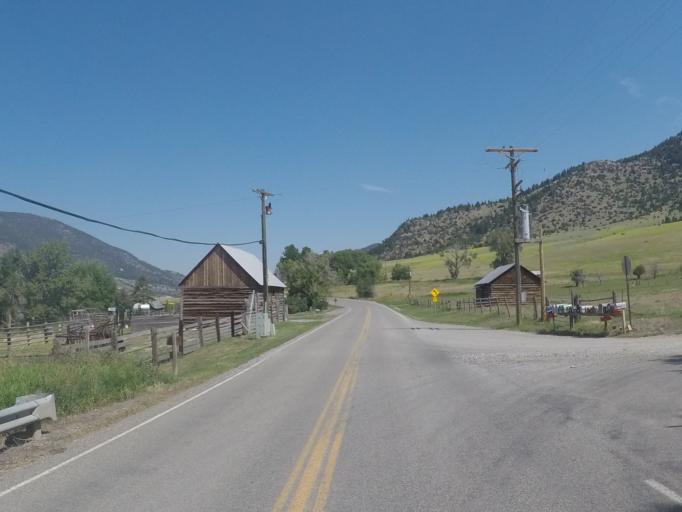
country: US
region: Montana
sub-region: Park County
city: Livingston
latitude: 45.5668
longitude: -110.5576
